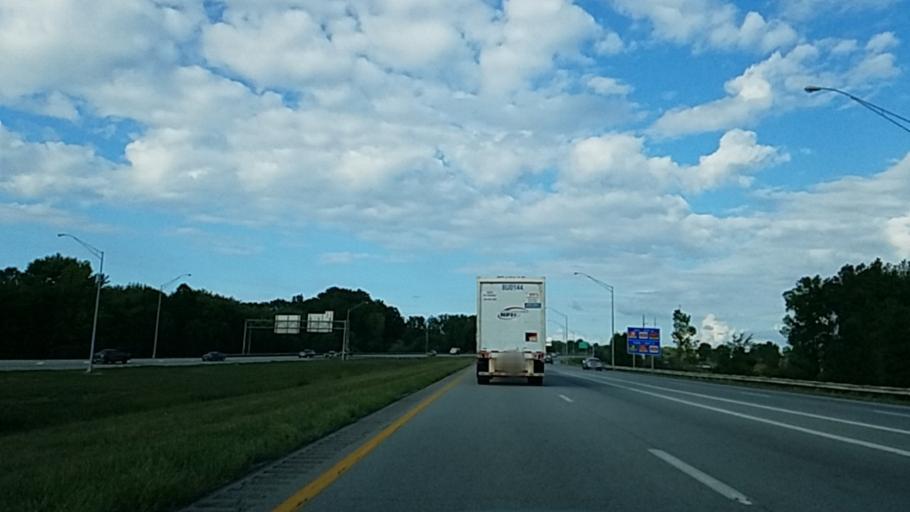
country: US
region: Ohio
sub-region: Lorain County
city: North Ridgeville
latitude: 41.3843
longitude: -81.9834
